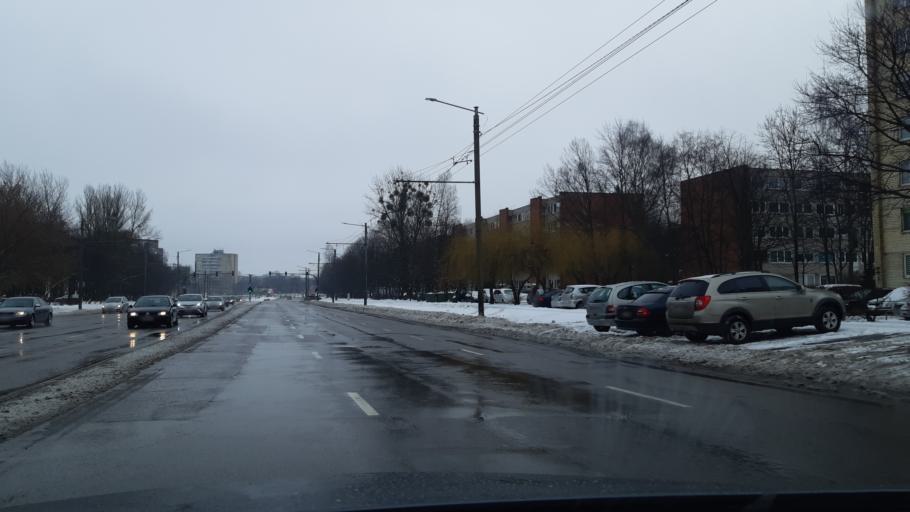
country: LT
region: Kauno apskritis
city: Dainava (Kaunas)
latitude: 54.9114
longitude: 23.9476
